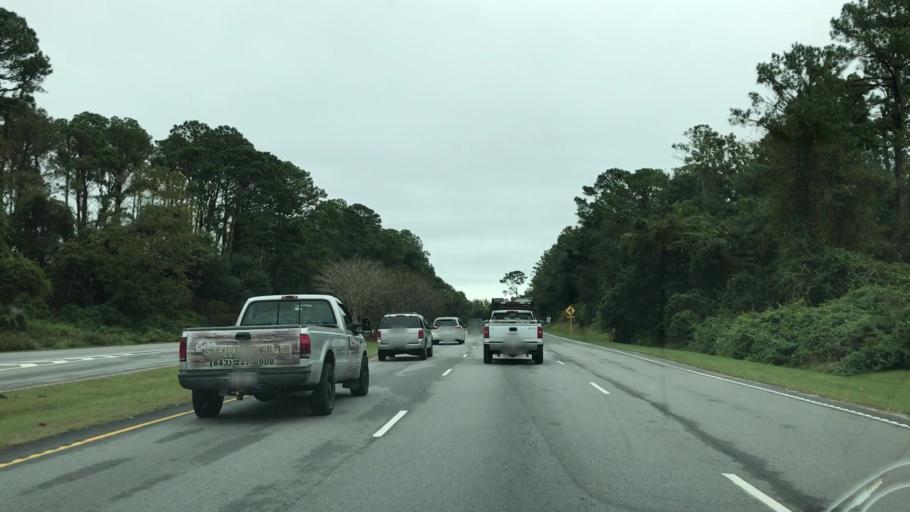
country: US
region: South Carolina
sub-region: Beaufort County
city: Hilton Head Island
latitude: 32.2183
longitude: -80.7729
